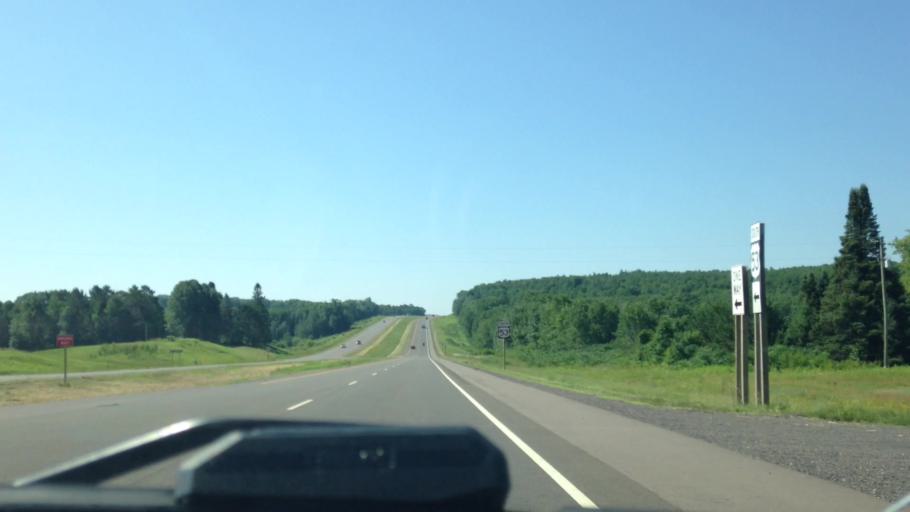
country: US
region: Wisconsin
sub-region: Washburn County
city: Spooner
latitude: 45.9808
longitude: -91.8277
